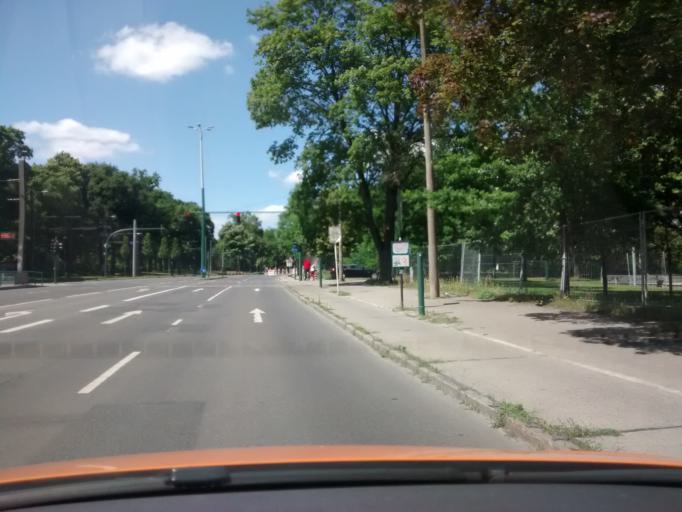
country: DE
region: Brandenburg
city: Potsdam
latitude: 52.3826
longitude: 13.0758
